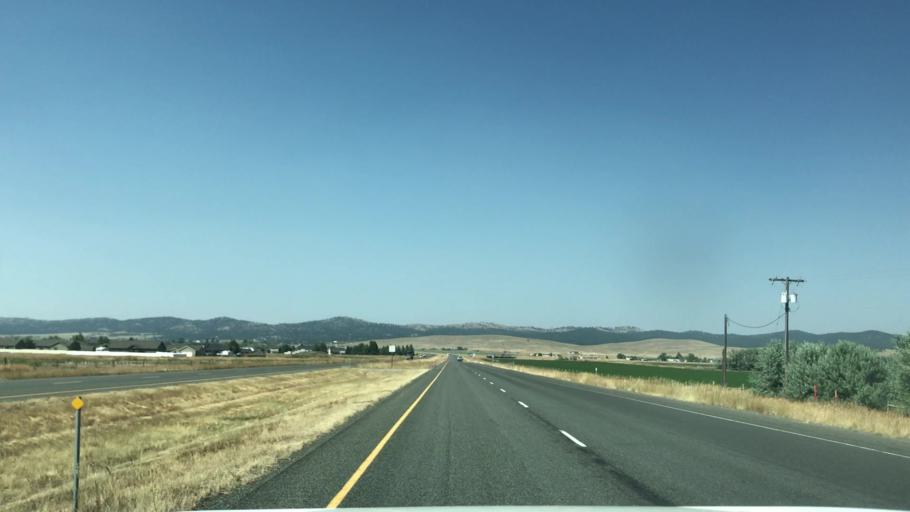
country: US
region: Montana
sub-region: Lewis and Clark County
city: Helena Valley Northwest
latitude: 46.7075
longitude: -112.0119
